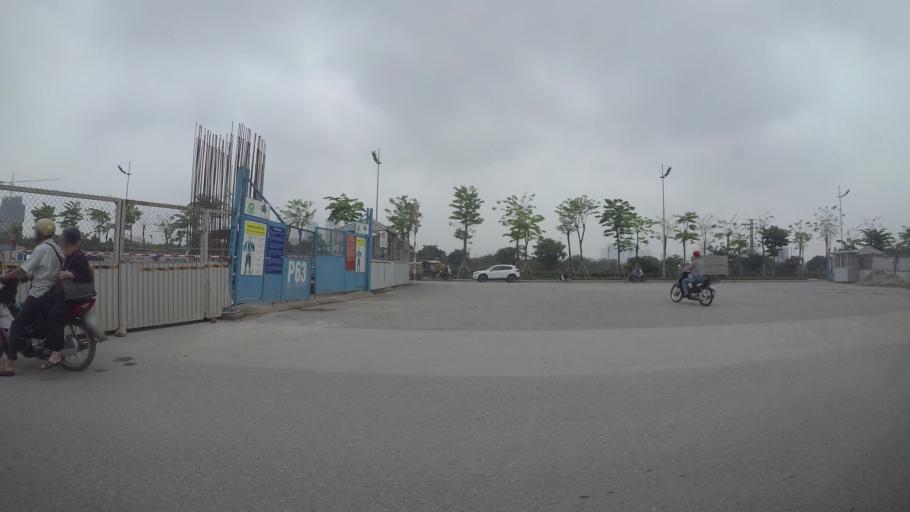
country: VN
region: Ha Noi
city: Tay Ho
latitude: 21.0628
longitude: 105.7839
